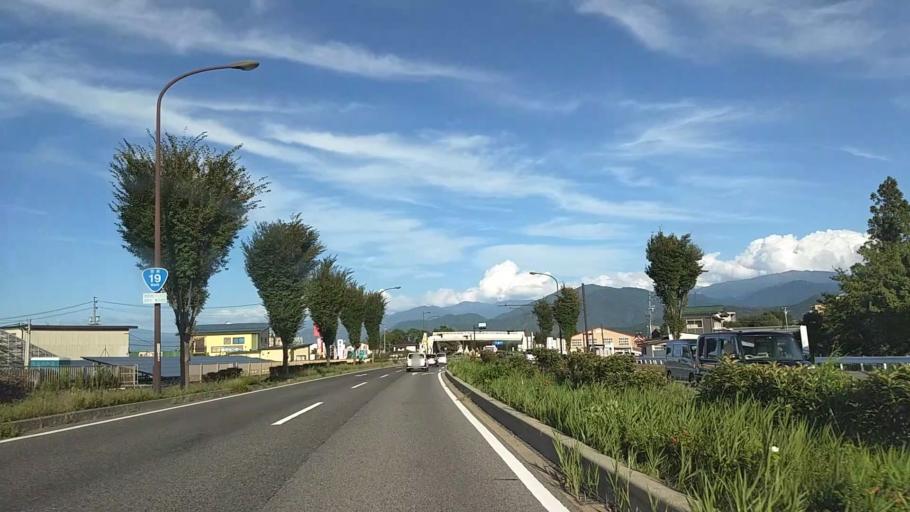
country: JP
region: Nagano
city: Nagano-shi
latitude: 36.6053
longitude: 138.1880
